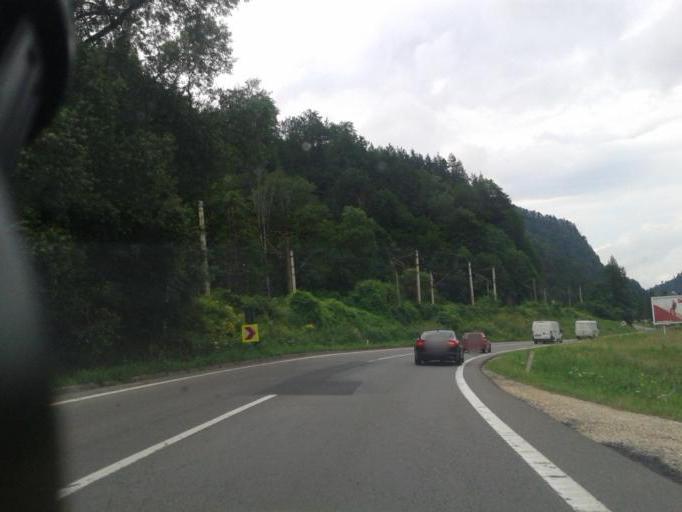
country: RO
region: Brasov
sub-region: Oras Predeal
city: Predeal
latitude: 45.5544
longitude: 25.5915
